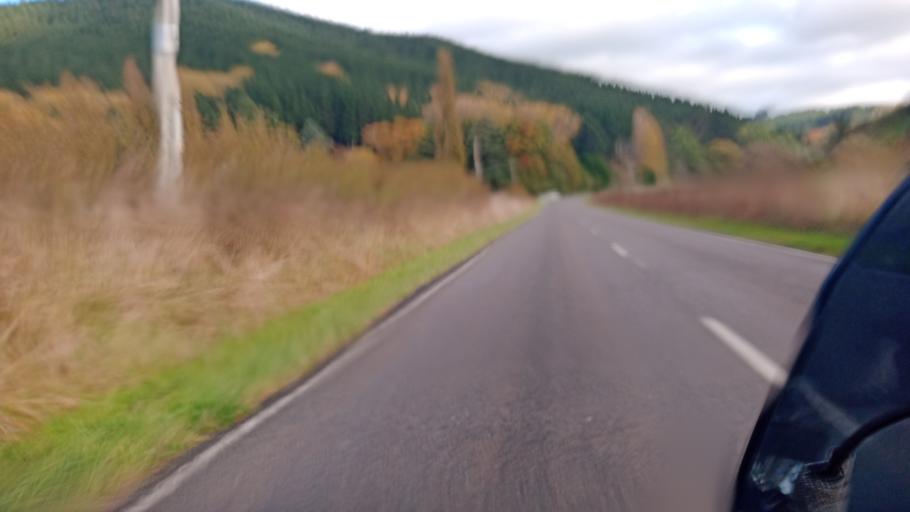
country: NZ
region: Gisborne
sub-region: Gisborne District
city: Gisborne
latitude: -38.5702
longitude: 177.7264
